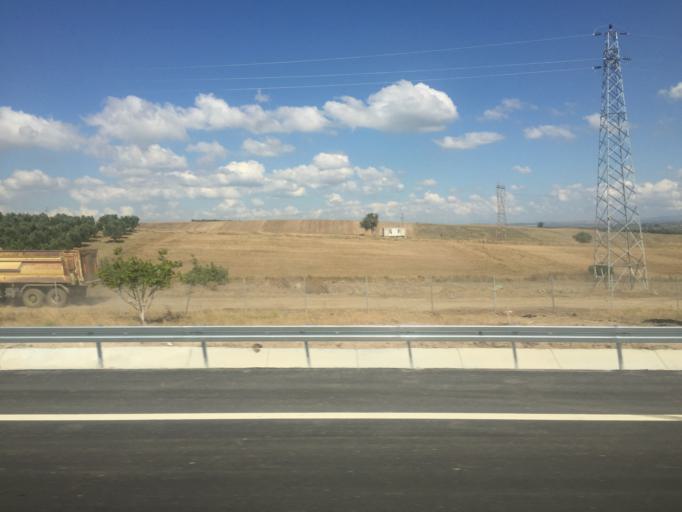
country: TR
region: Balikesir
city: Gobel
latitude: 40.0458
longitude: 28.2253
